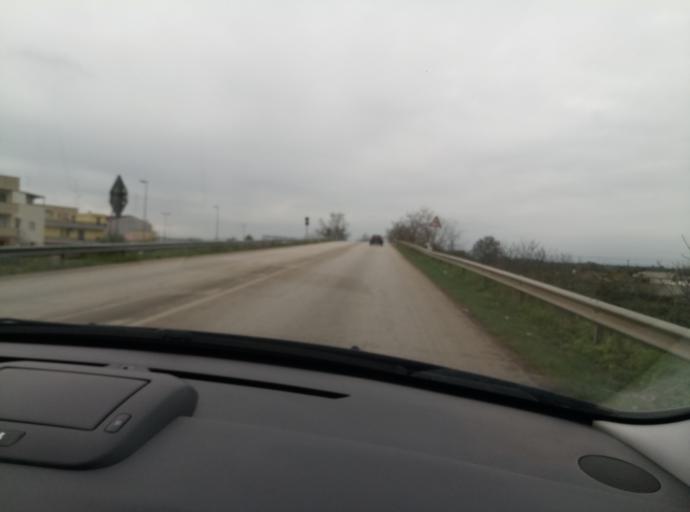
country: IT
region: Apulia
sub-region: Provincia di Bari
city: Acquaviva delle Fonti
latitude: 40.9039
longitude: 16.8392
